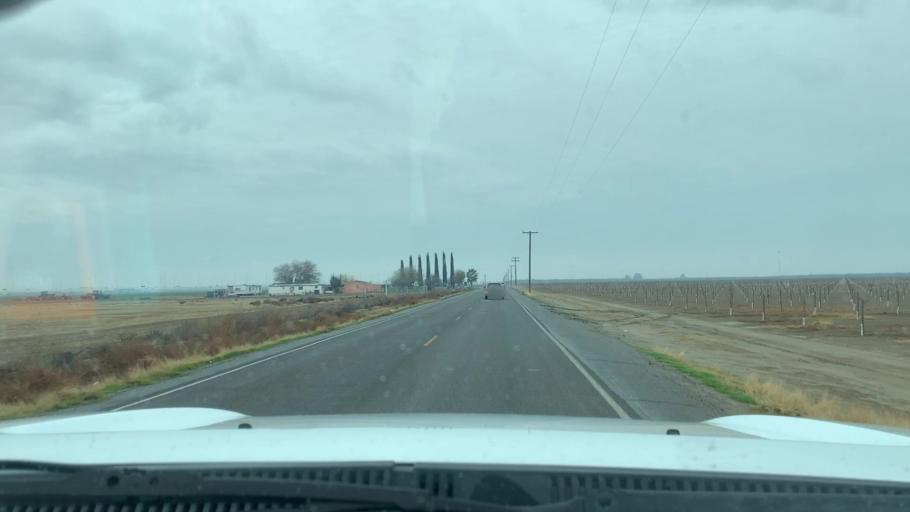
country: US
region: California
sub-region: Kern County
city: Delano
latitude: 35.7612
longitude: -119.3420
